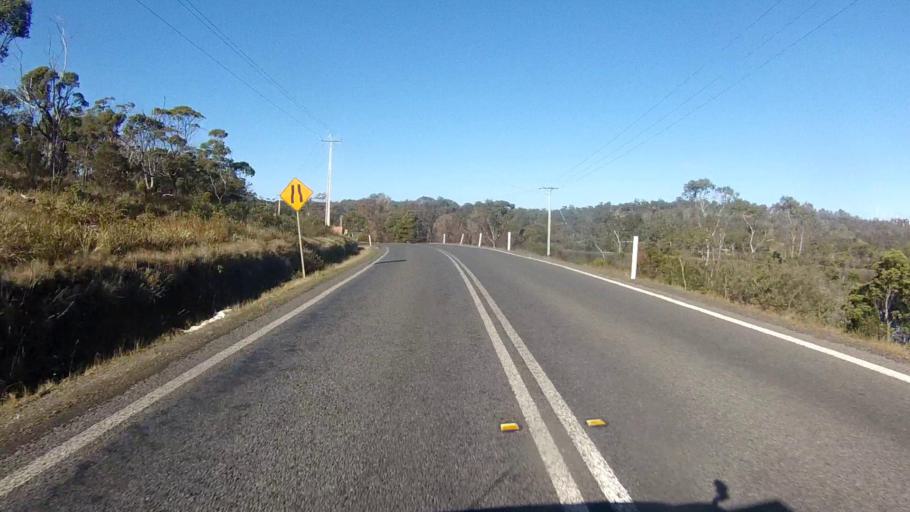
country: AU
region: Tasmania
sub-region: Sorell
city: Sorell
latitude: -42.9397
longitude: 147.8614
